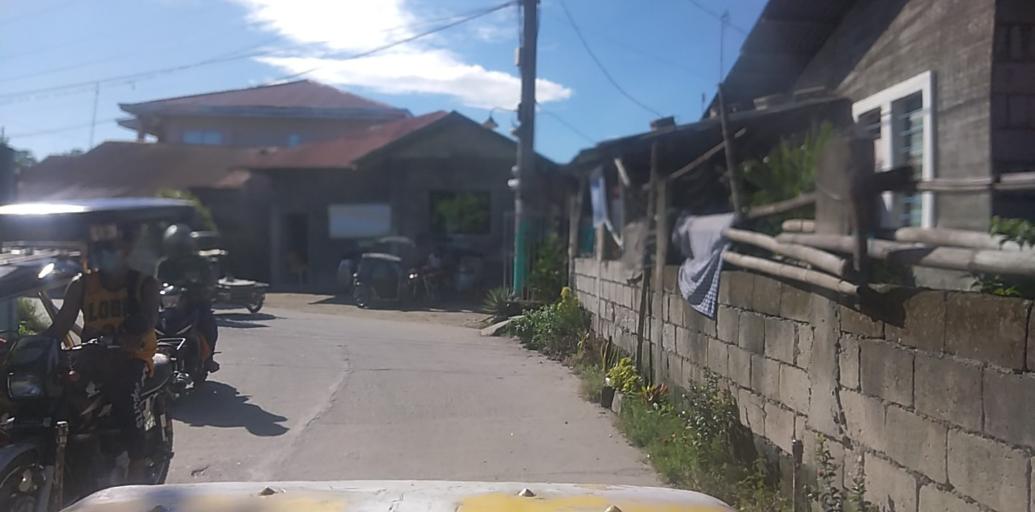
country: PH
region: Central Luzon
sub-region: Province of Pampanga
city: San Patricio
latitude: 15.1120
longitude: 120.7115
